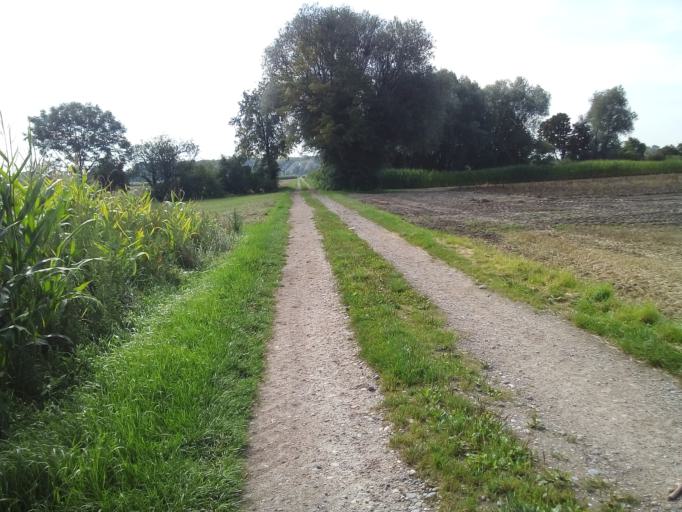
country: DE
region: Bavaria
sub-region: Upper Bavaria
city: Ismaning
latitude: 48.2176
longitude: 11.6982
